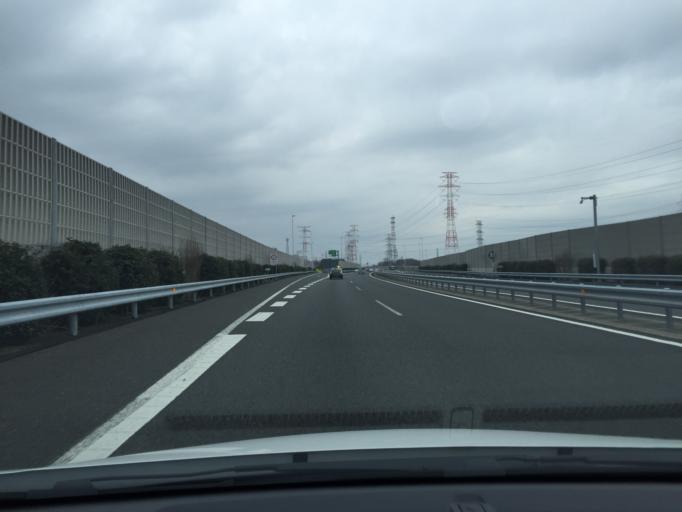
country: JP
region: Saitama
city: Sakado
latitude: 35.9695
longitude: 139.4467
